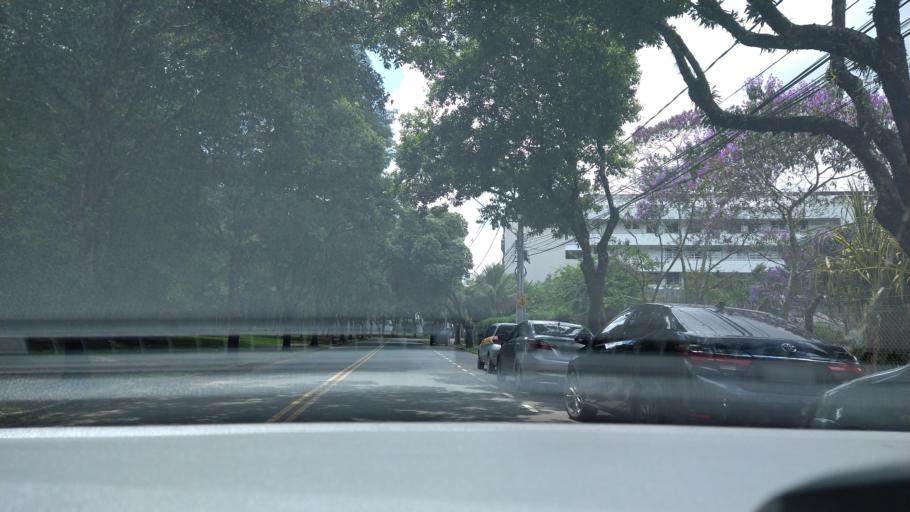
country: BR
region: Minas Gerais
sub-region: Vicosa
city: Vicosa
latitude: -20.7569
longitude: -42.8731
